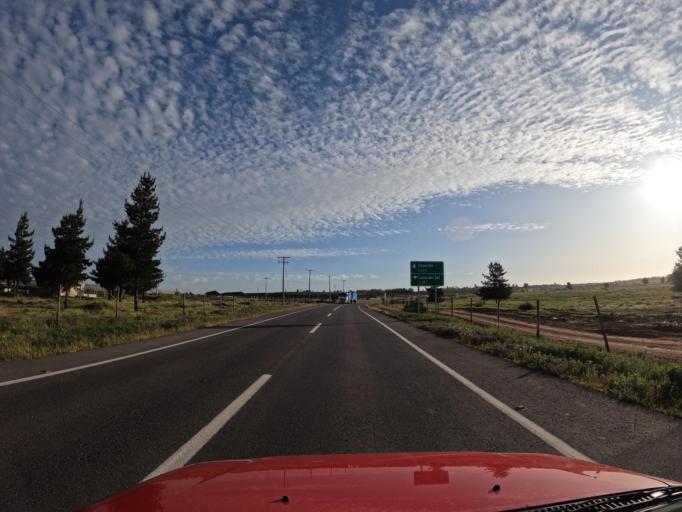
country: CL
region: Valparaiso
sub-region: San Antonio Province
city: San Antonio
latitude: -34.0712
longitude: -71.6305
